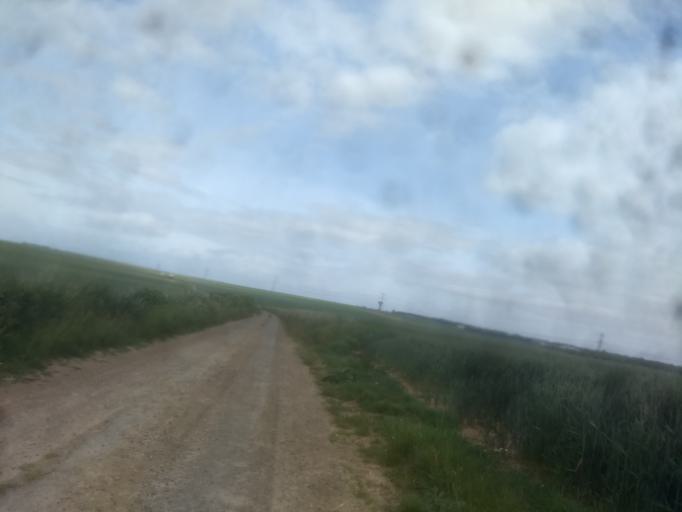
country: FR
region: Nord-Pas-de-Calais
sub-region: Departement du Pas-de-Calais
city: Feuchy
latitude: 50.2818
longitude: 2.8385
